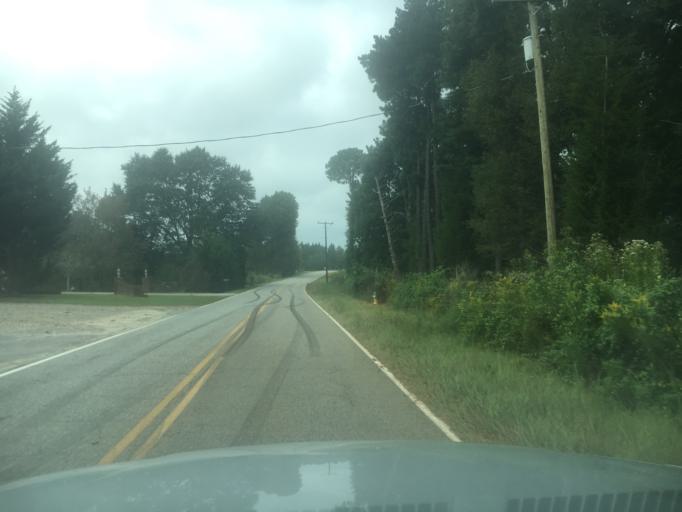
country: US
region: South Carolina
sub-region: Spartanburg County
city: Landrum
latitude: 35.1611
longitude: -82.0935
